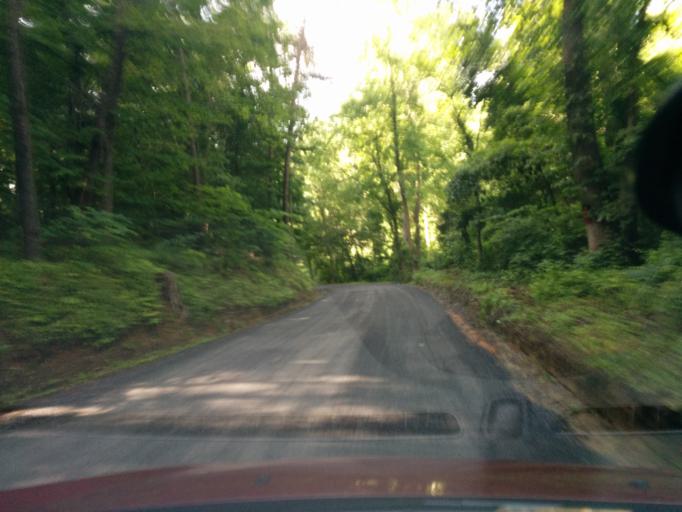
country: US
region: Virginia
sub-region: City of Lexington
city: Lexington
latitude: 37.7800
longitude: -79.4984
